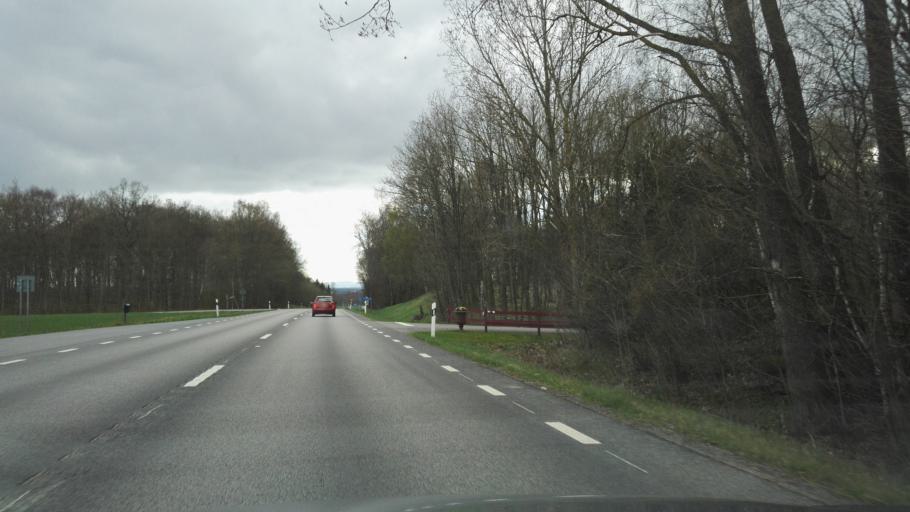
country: SE
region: Skane
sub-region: Sjobo Kommun
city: Sjoebo
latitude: 55.6595
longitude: 13.7064
